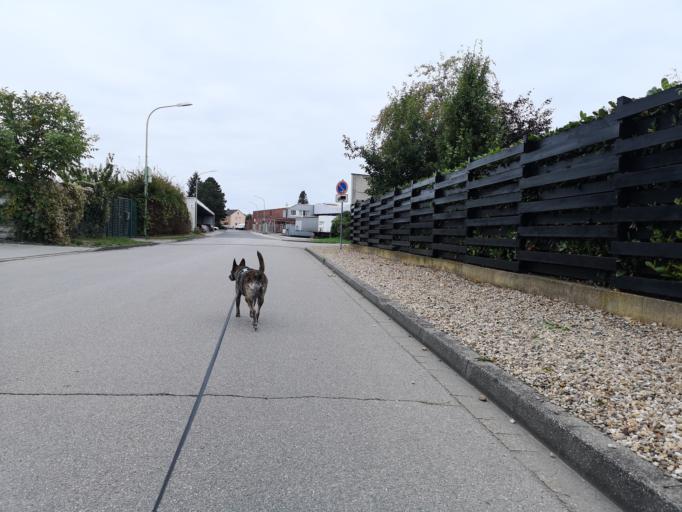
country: DE
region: North Rhine-Westphalia
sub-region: Regierungsbezirk Koln
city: Kreuzau
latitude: 50.7484
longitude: 6.4944
